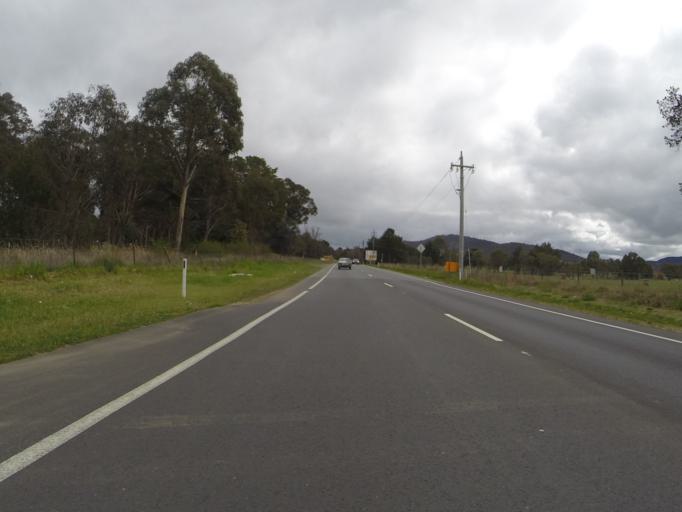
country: AU
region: Australian Capital Territory
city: Canberra
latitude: -35.2954
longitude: 149.1735
